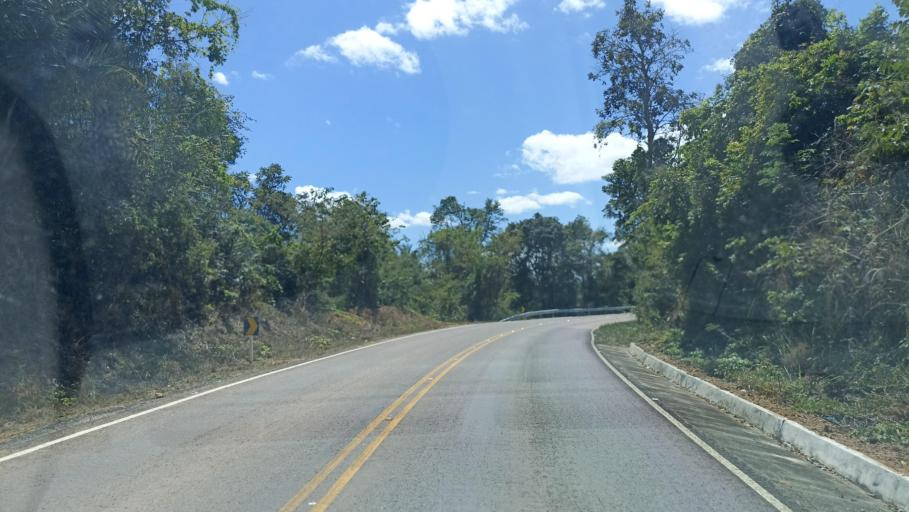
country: BR
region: Bahia
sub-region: Andarai
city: Vera Cruz
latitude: -12.7525
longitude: -41.3287
